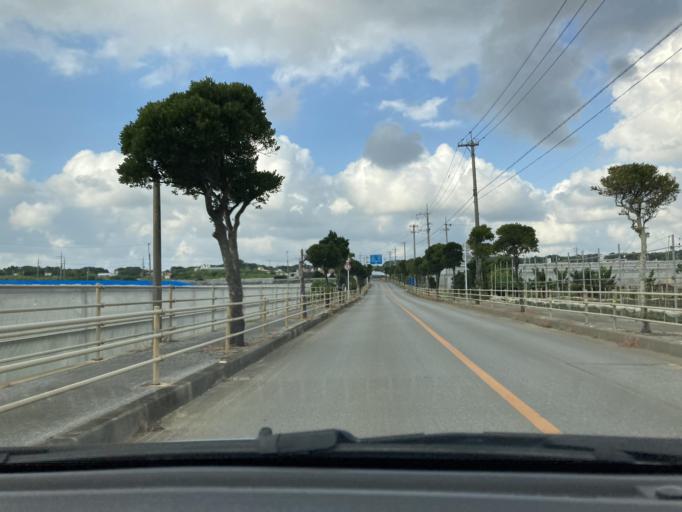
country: JP
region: Okinawa
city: Itoman
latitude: 26.1009
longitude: 127.6658
